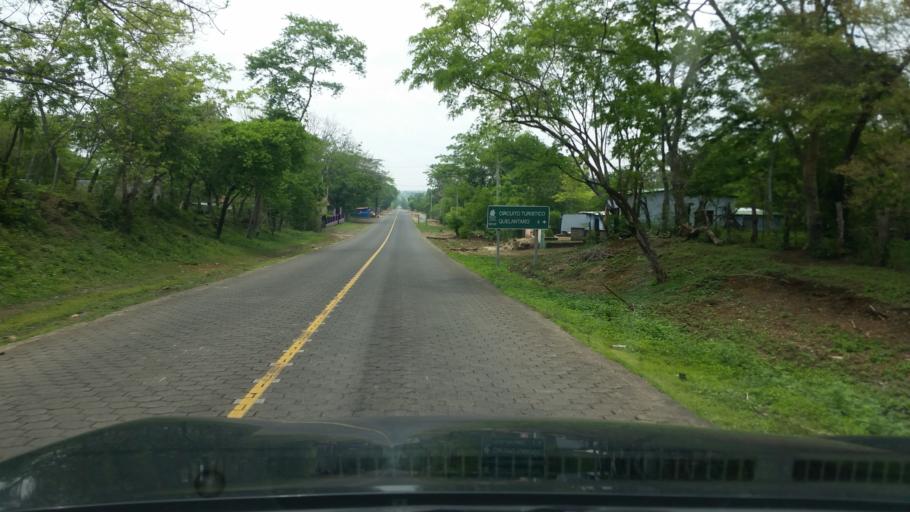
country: NI
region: Managua
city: Carlos Fonseca Amador
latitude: 11.9412
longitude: -86.5082
